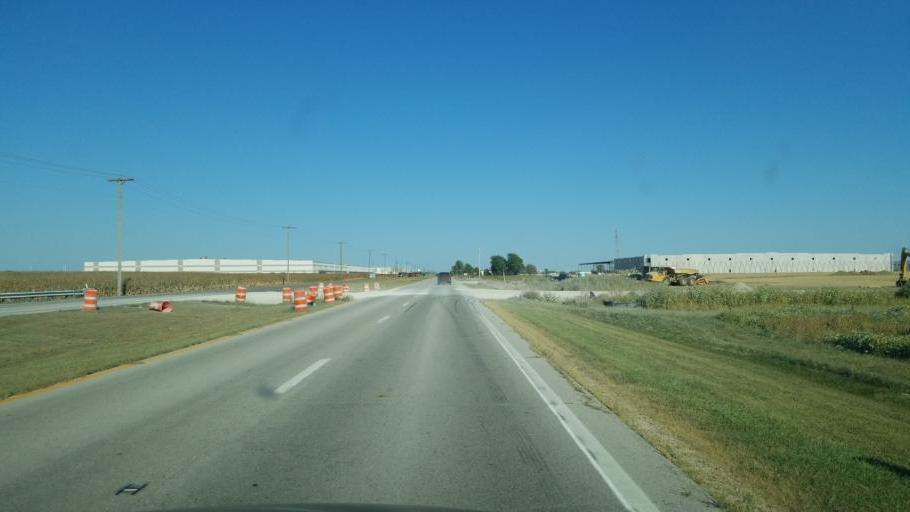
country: US
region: Ohio
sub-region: Madison County
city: West Jefferson
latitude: 39.9410
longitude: -83.3376
